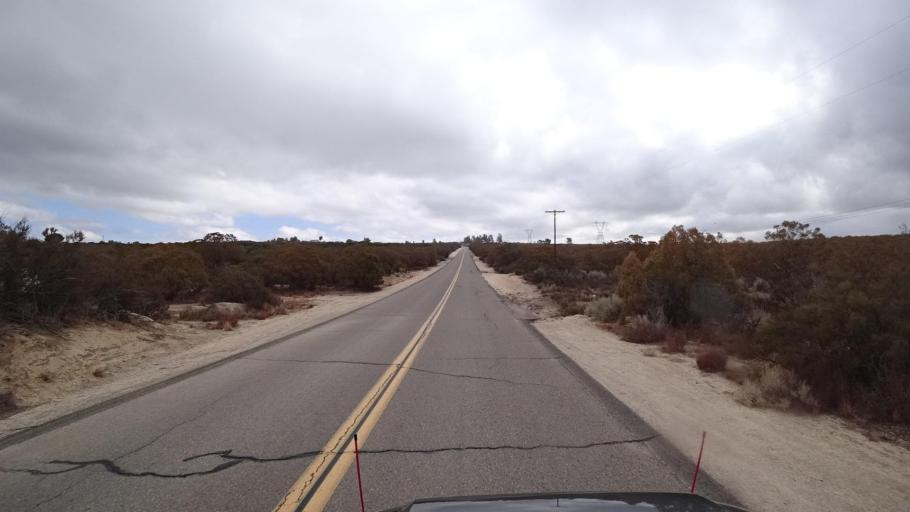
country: US
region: California
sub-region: San Diego County
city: Campo
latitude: 32.6052
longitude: -116.3411
